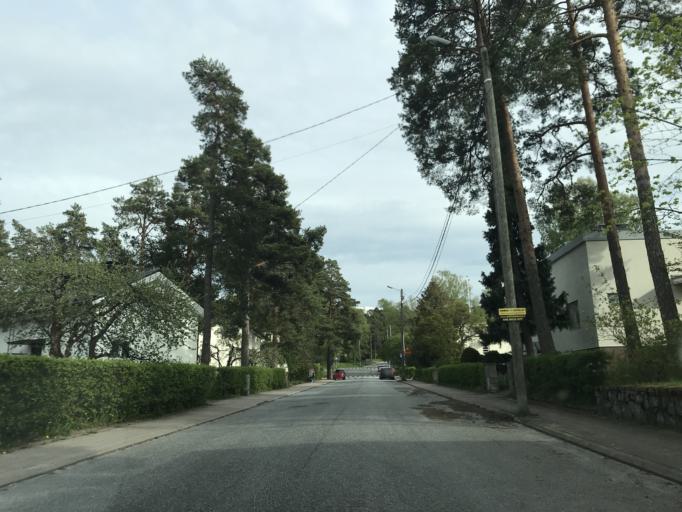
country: FI
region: Varsinais-Suomi
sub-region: Turku
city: Turku
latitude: 60.4373
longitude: 22.3006
